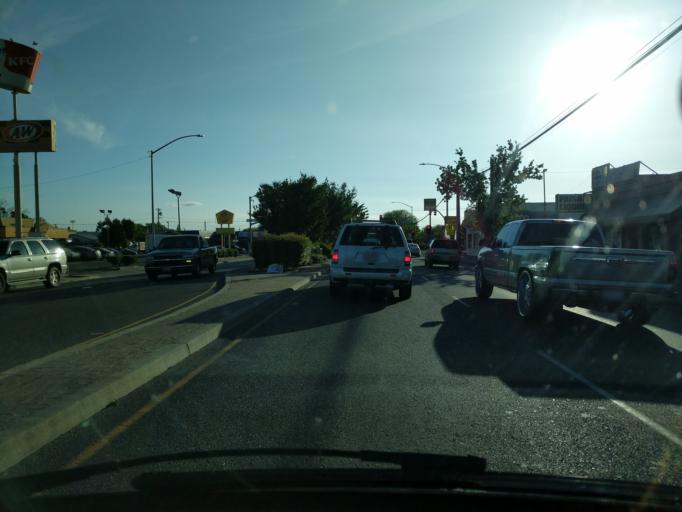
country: US
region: California
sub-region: San Joaquin County
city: Stockton
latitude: 37.9392
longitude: -121.2850
